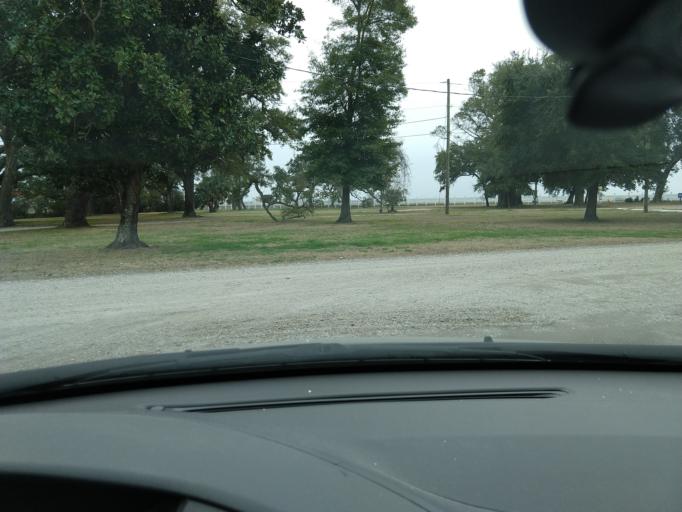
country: US
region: Mississippi
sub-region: Harrison County
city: Biloxi
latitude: 30.3930
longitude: -88.9691
